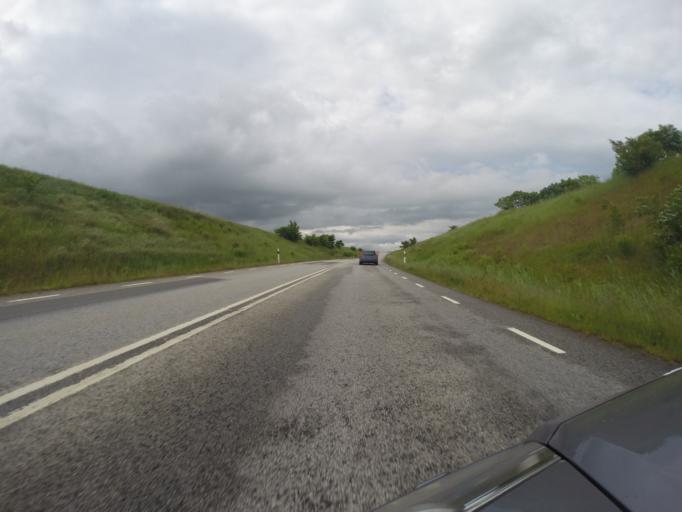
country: SE
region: Skane
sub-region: Landskrona
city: Asmundtorp
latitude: 55.8480
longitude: 12.9677
